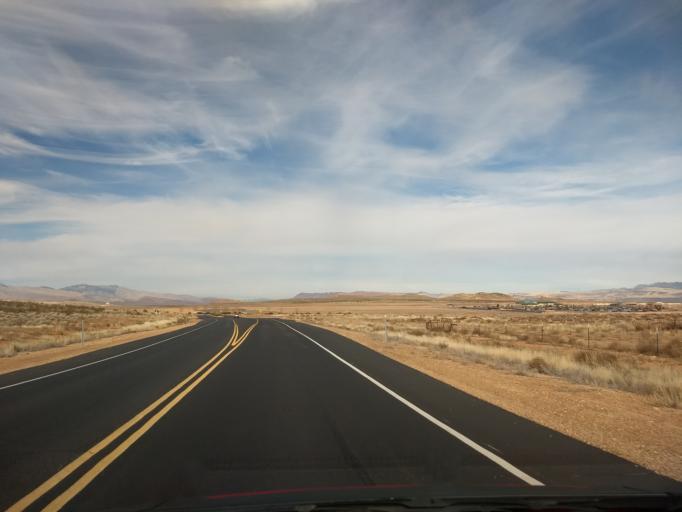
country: US
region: Utah
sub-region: Washington County
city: Washington
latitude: 37.0226
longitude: -113.5051
